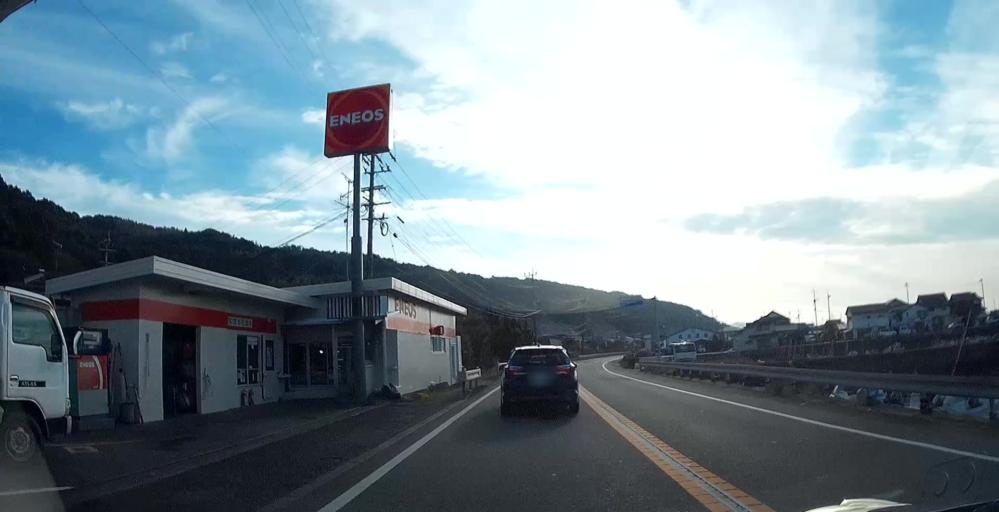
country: JP
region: Kumamoto
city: Uto
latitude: 32.6946
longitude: 130.5652
